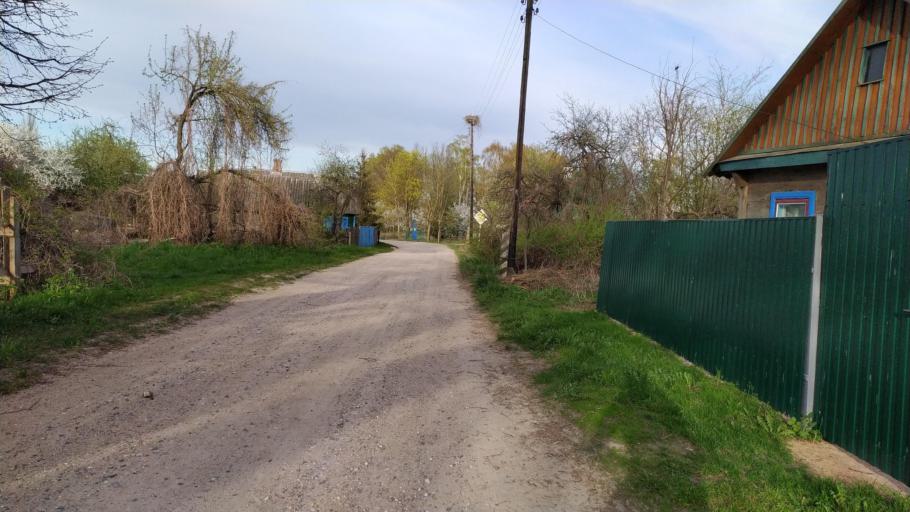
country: BY
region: Brest
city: Kamyanyets
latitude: 52.4094
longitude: 23.6714
